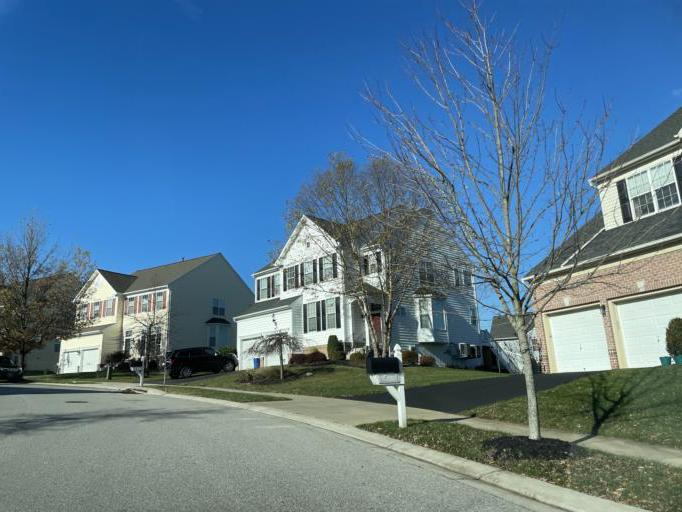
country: US
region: Maryland
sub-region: Baltimore County
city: Pikesville
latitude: 39.3746
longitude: -76.6690
